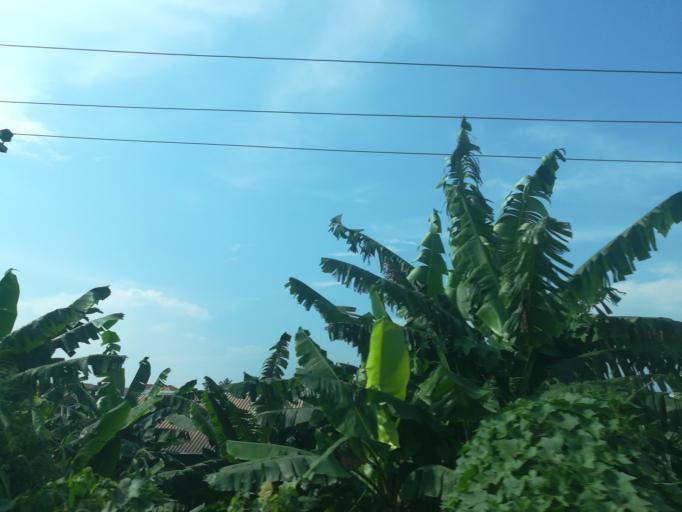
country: NG
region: Lagos
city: Ikorodu
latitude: 6.6304
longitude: 3.5175
